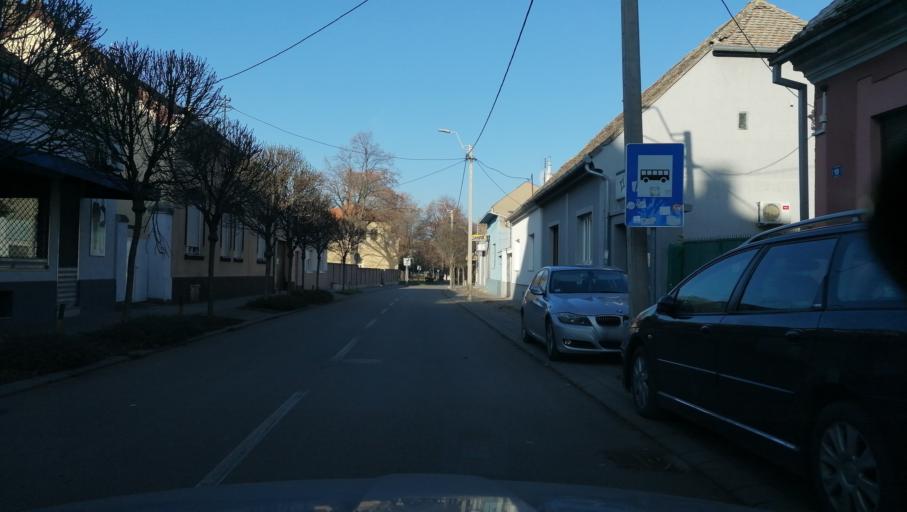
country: RS
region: Autonomna Pokrajina Vojvodina
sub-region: Sremski Okrug
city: Sremska Mitrovica
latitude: 44.9689
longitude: 19.6127
